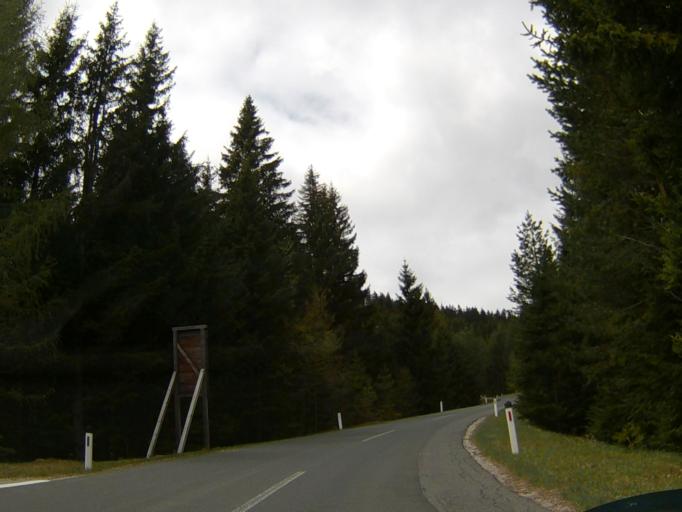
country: AT
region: Carinthia
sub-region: Politischer Bezirk Villach Land
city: Arnoldstein
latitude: 46.5887
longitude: 13.7561
